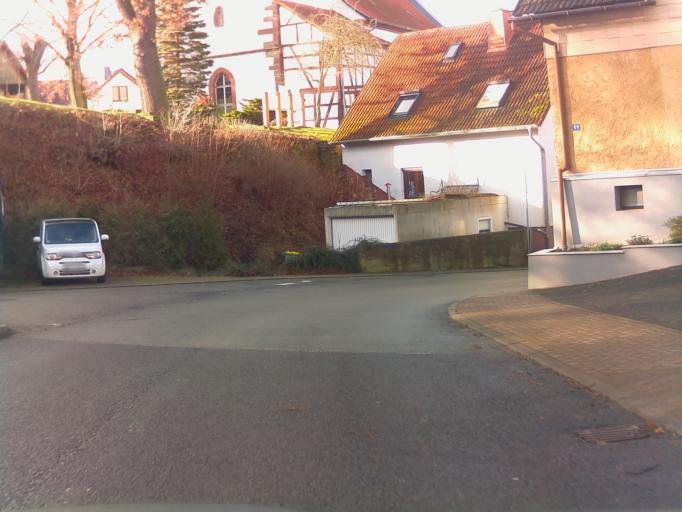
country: DE
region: Thuringia
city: Wiesenthal
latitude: 50.7023
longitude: 10.1697
